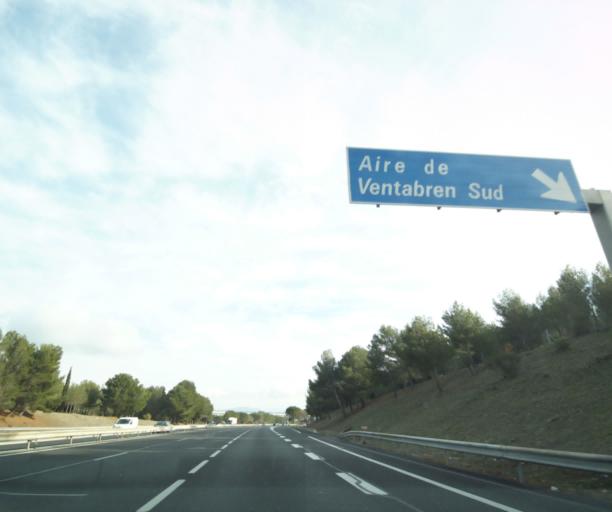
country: FR
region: Provence-Alpes-Cote d'Azur
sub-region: Departement des Bouches-du-Rhone
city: Ventabren
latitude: 43.5519
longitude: 5.3159
